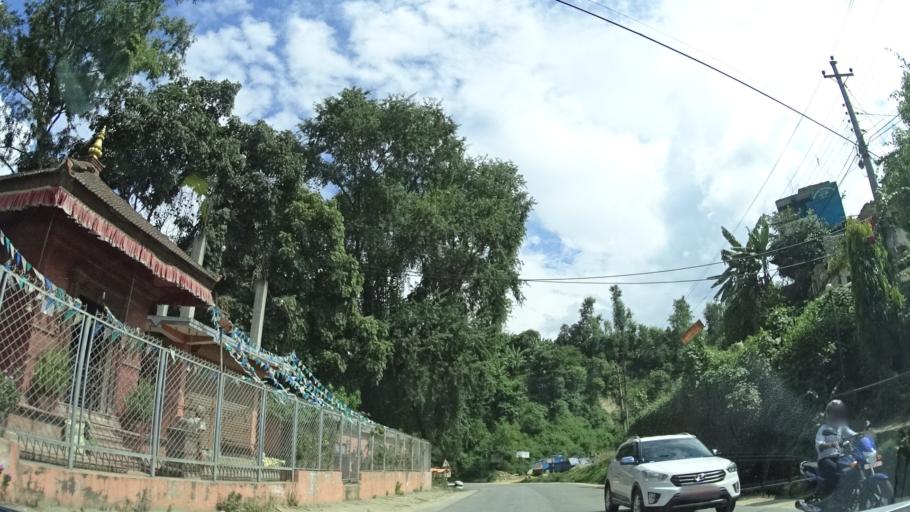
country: NP
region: Central Region
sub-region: Narayani Zone
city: Hitura
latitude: 27.8052
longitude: 84.8821
